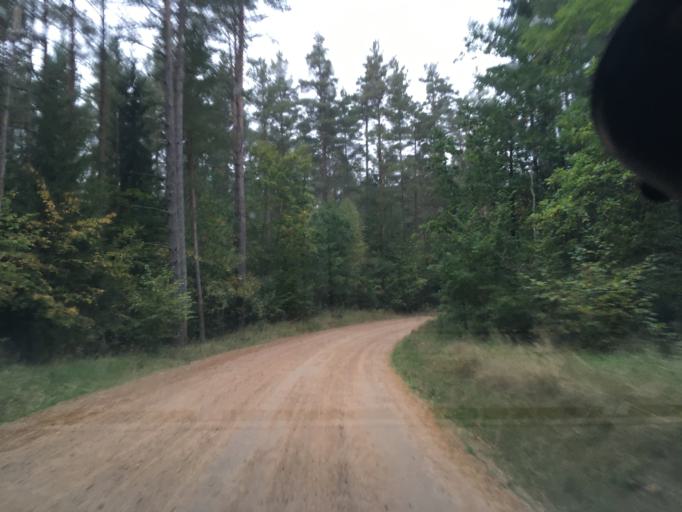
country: LV
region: Kuldigas Rajons
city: Kuldiga
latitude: 57.0111
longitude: 21.9831
